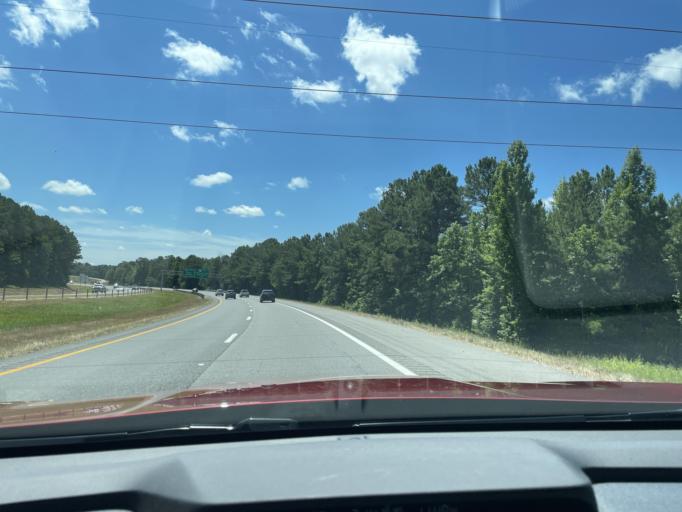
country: US
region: Arkansas
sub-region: Jefferson County
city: White Hall
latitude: 34.2489
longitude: -92.1015
